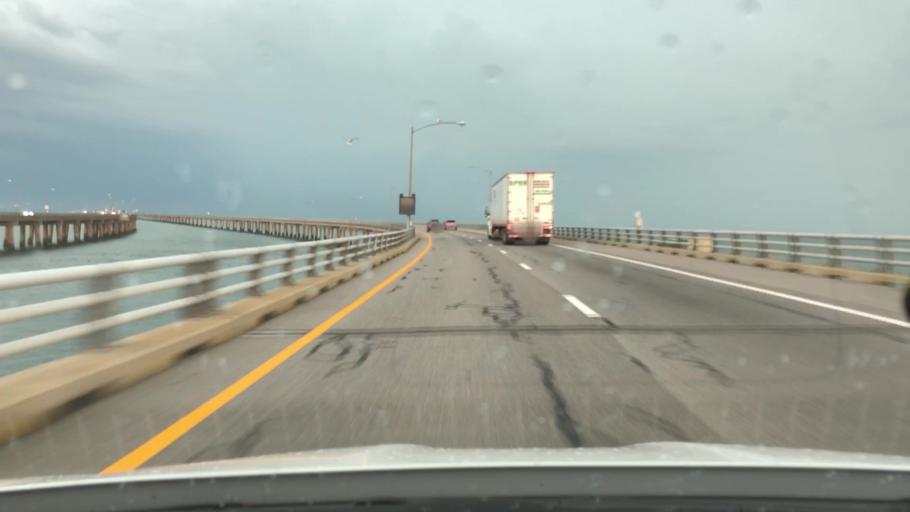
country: US
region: Virginia
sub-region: City of Virginia Beach
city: Virginia Beach
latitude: 37.0313
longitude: -76.0855
